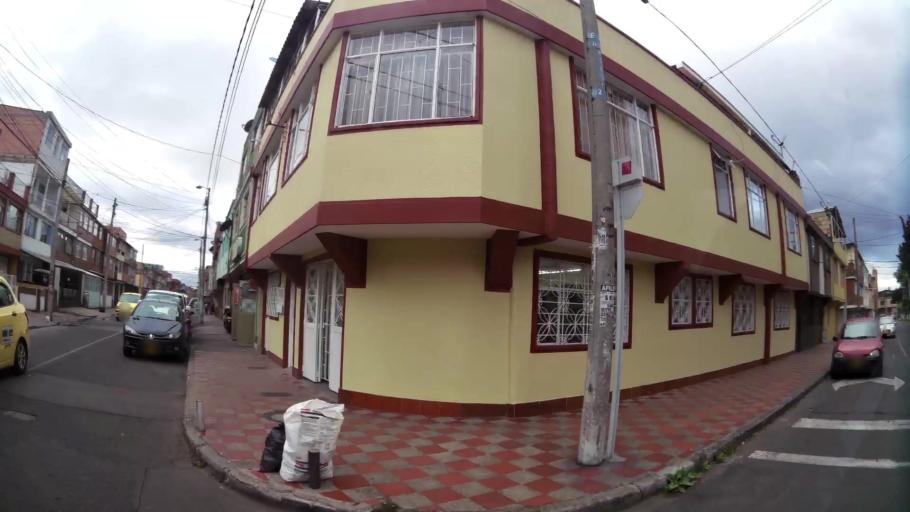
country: CO
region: Bogota D.C.
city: Bogota
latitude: 4.6003
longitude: -74.1055
